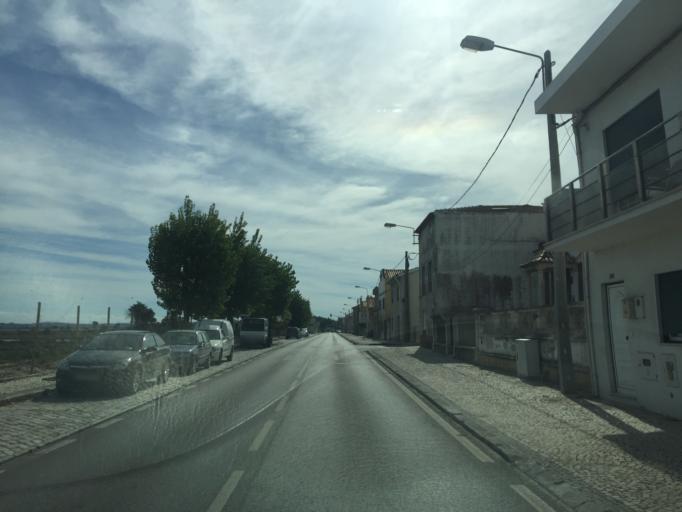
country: PT
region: Coimbra
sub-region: Figueira da Foz
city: Figueira da Foz
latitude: 40.1283
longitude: -8.8534
